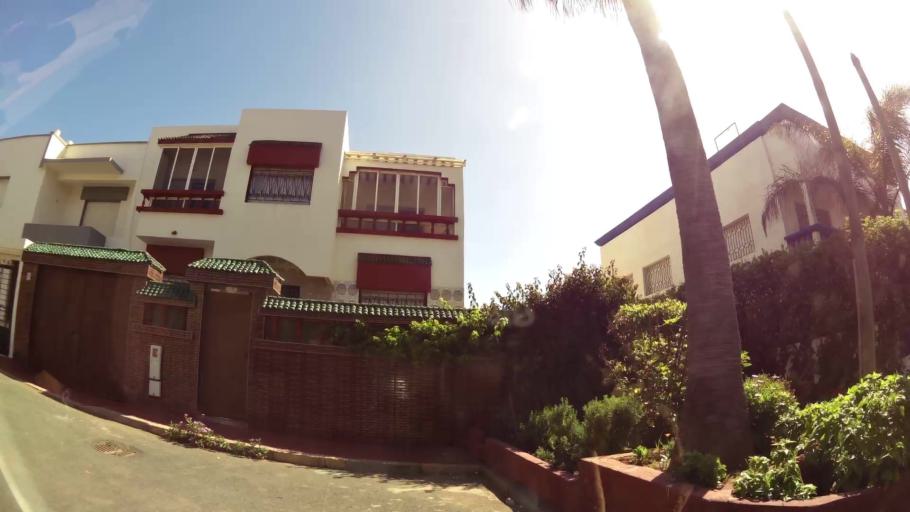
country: MA
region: Rabat-Sale-Zemmour-Zaer
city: Sale
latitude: 34.0695
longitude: -6.8033
